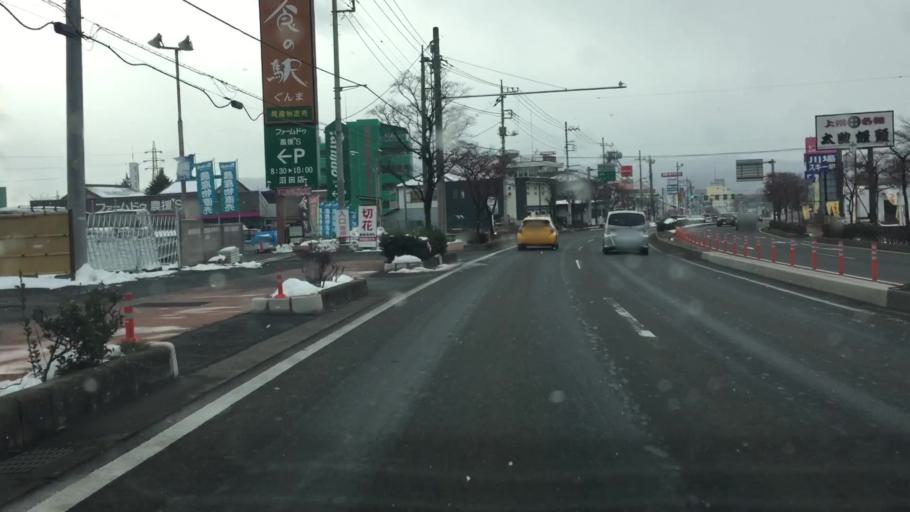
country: JP
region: Gunma
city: Numata
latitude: 36.6554
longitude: 139.0745
